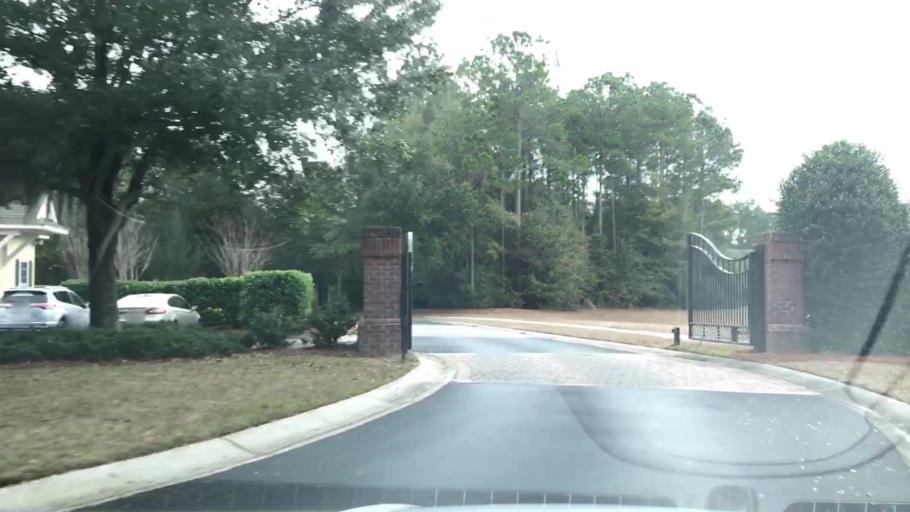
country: US
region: South Carolina
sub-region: Beaufort County
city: Bluffton
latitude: 32.2763
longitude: -80.9297
